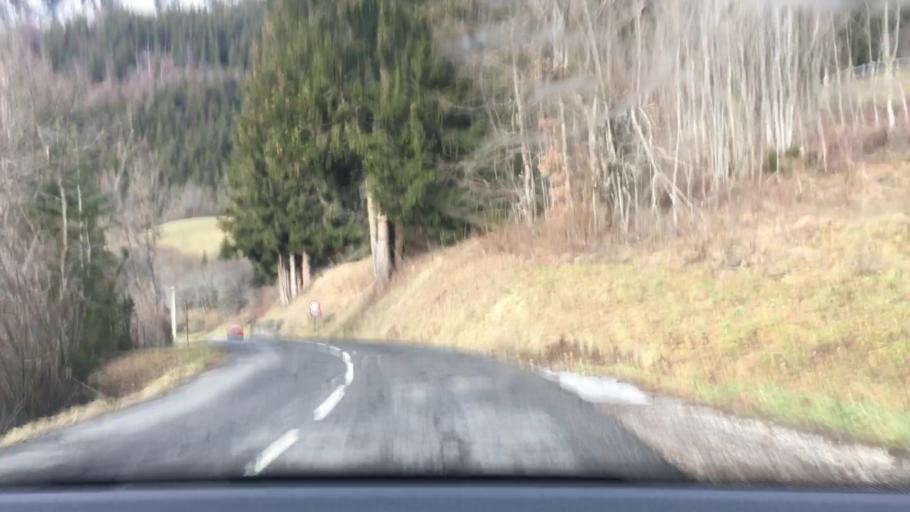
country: FR
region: Rhone-Alpes
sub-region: Departement de la Haute-Savoie
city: Abondance
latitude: 46.2790
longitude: 6.6363
